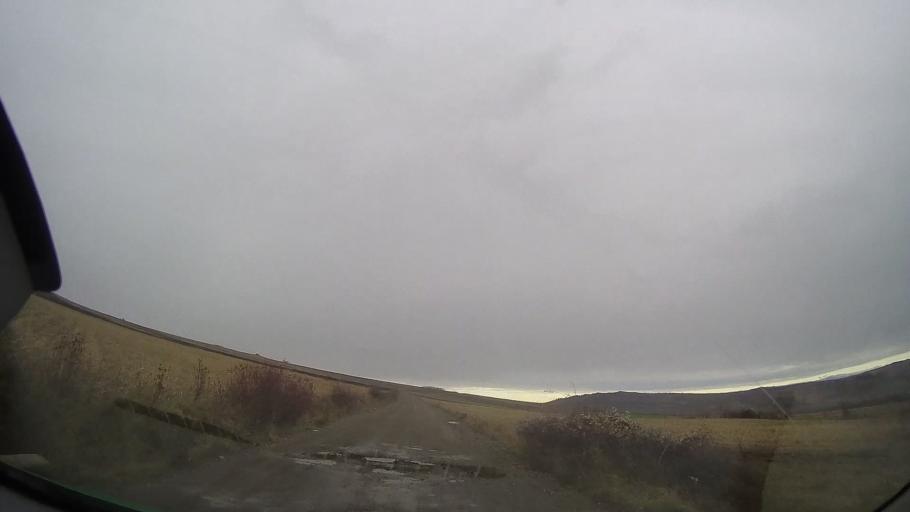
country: RO
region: Mures
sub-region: Comuna Ceausu de Campie
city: Ceausu de Campie
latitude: 46.6607
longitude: 24.4873
